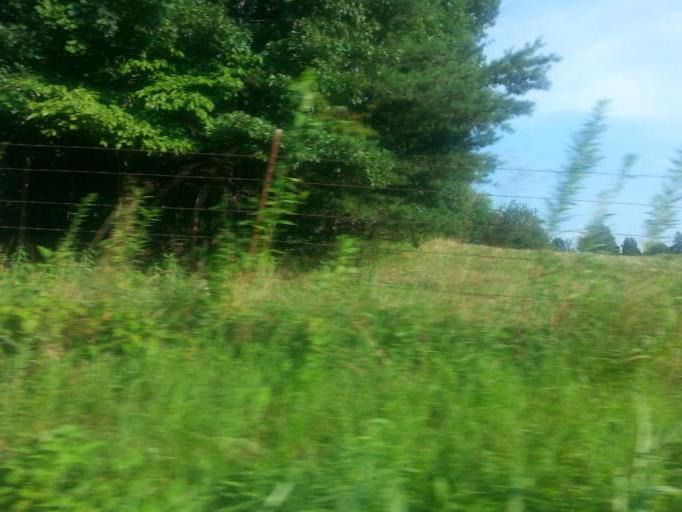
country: US
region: Tennessee
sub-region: Blount County
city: Wildwood
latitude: 35.7970
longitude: -83.8553
